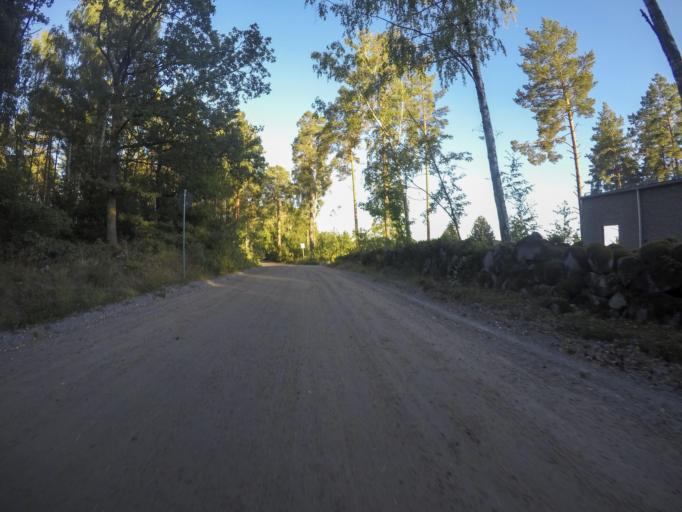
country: SE
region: Vaestmanland
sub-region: Vasteras
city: Vasteras
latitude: 59.5537
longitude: 16.6688
